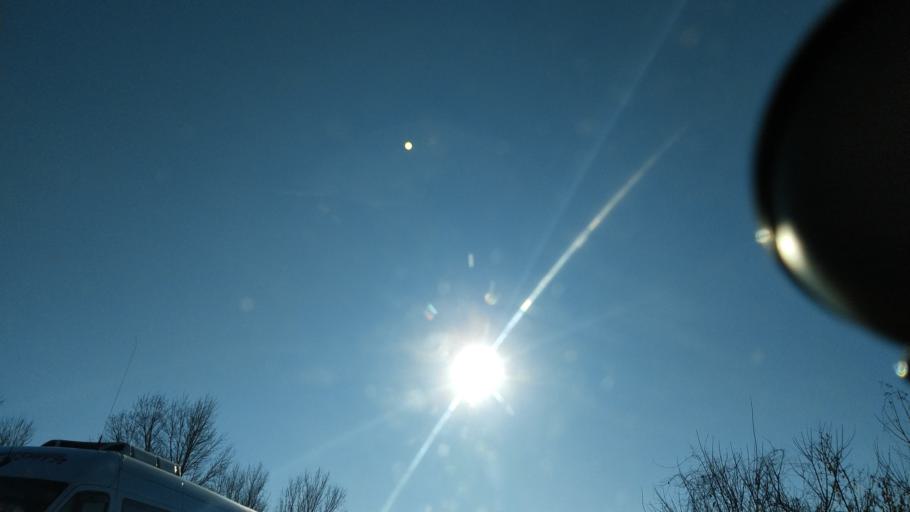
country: RO
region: Iasi
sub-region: Comuna Butea
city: Butea
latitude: 47.0857
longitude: 26.9018
